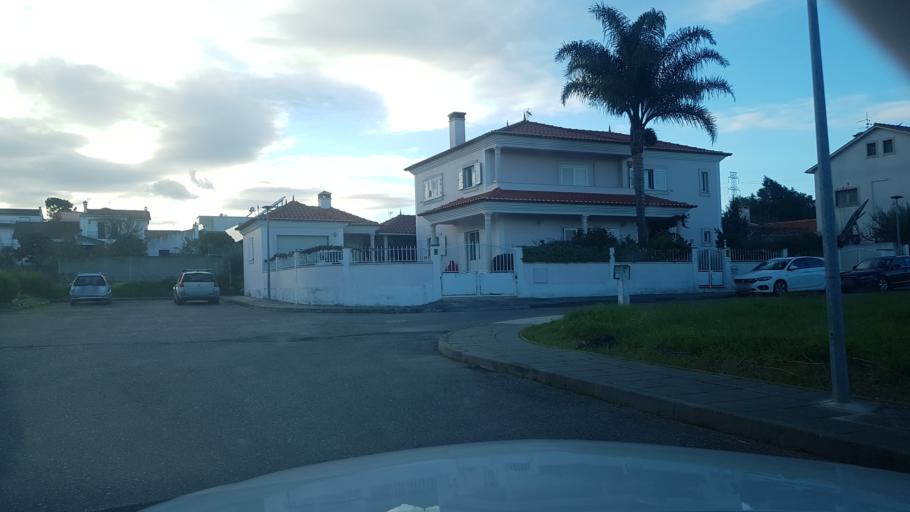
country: PT
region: Santarem
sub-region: Entroncamento
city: Entroncamento
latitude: 39.4757
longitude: -8.4792
